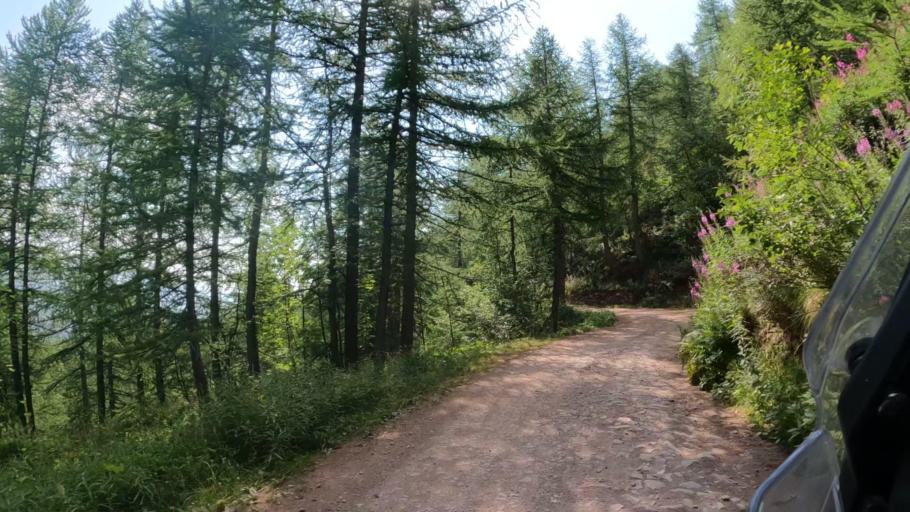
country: IT
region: Piedmont
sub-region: Provincia di Cuneo
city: Briga Alta
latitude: 44.1207
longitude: 7.6923
